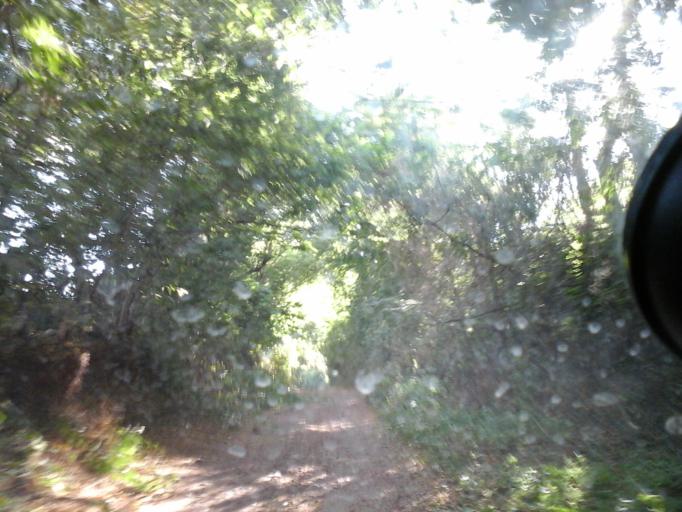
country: CO
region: Cesar
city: San Diego
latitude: 10.2433
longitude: -73.1357
